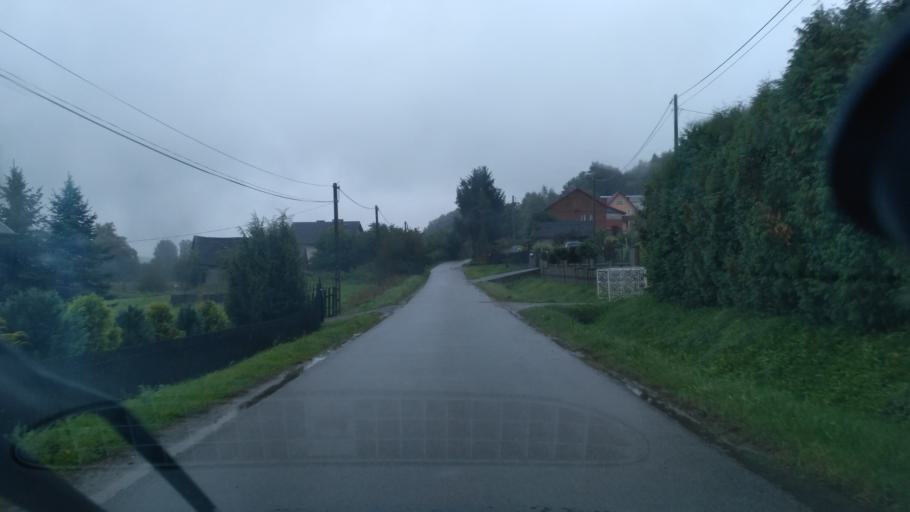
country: PL
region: Subcarpathian Voivodeship
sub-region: Powiat ropczycko-sedziszowski
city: Niedzwiada
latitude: 50.0128
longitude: 21.5474
